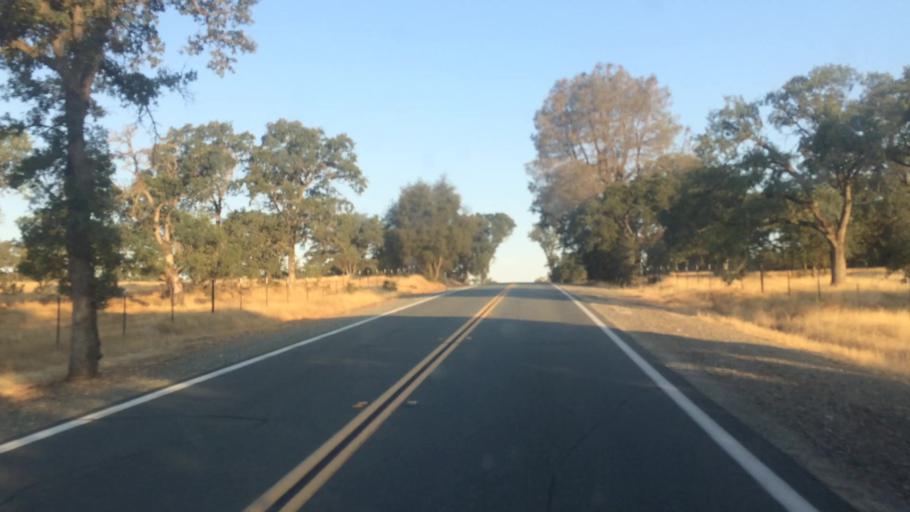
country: US
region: California
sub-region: Amador County
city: Ione
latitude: 38.3722
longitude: -120.9917
